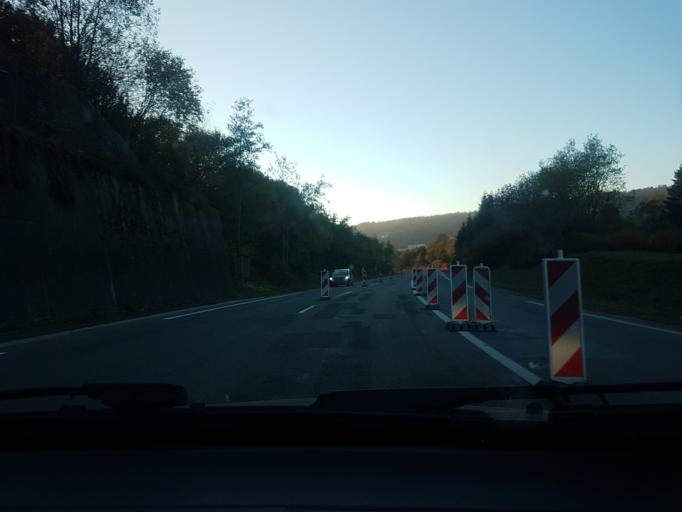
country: FR
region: Franche-Comte
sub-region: Departement du Doubs
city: Villers-le-Lac
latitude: 47.0578
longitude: 6.6835
